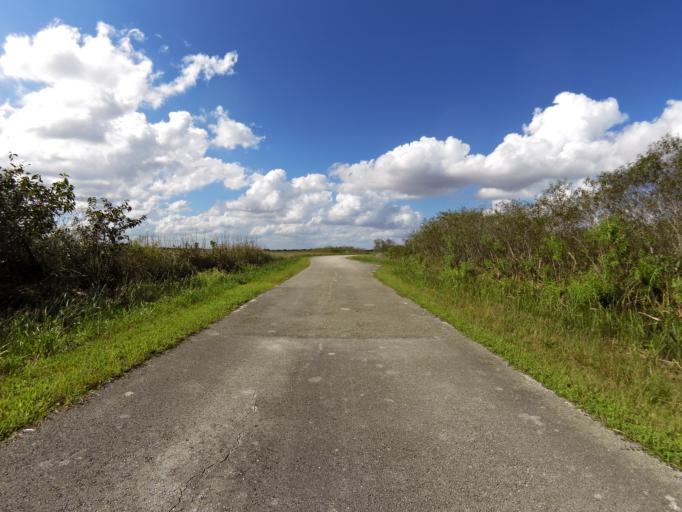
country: US
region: Florida
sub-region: Miami-Dade County
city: The Hammocks
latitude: 25.6728
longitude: -80.7607
